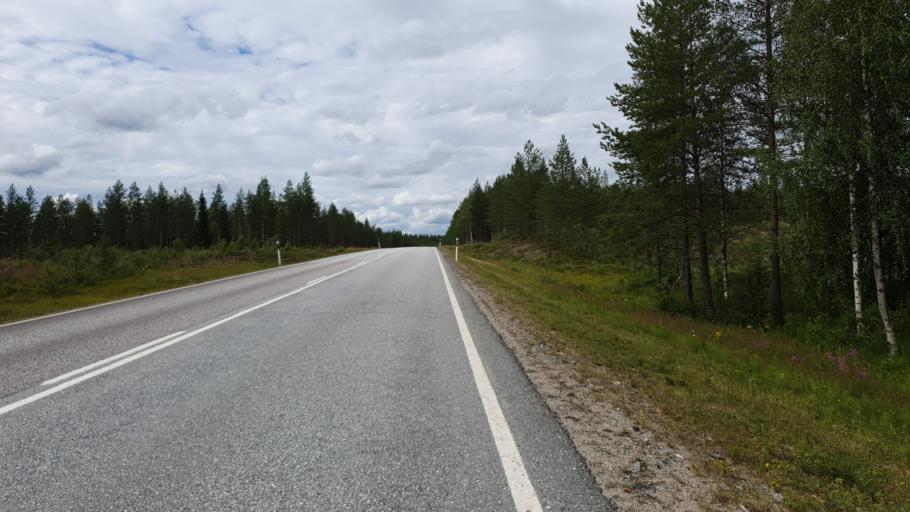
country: FI
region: Kainuu
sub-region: Kehys-Kainuu
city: Kuhmo
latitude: 64.4822
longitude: 29.7780
